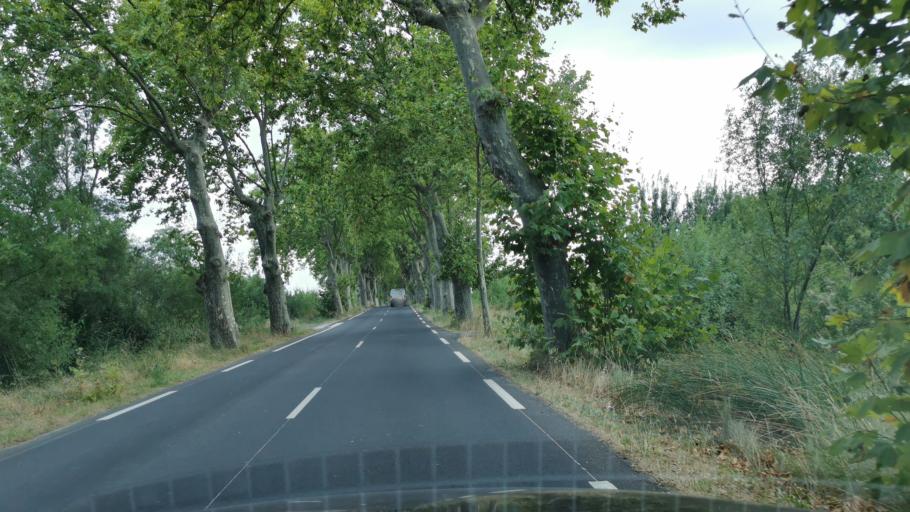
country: FR
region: Languedoc-Roussillon
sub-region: Departement de l'Herault
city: Capestang
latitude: 43.3217
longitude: 3.0356
